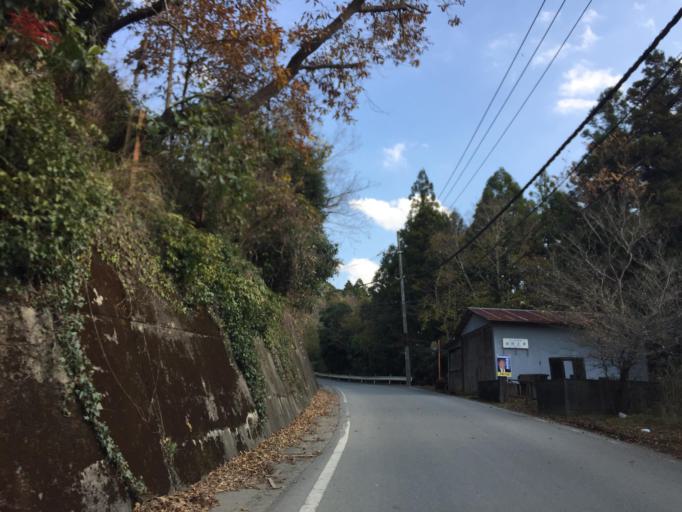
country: JP
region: Wakayama
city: Iwade
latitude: 34.1486
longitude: 135.3605
